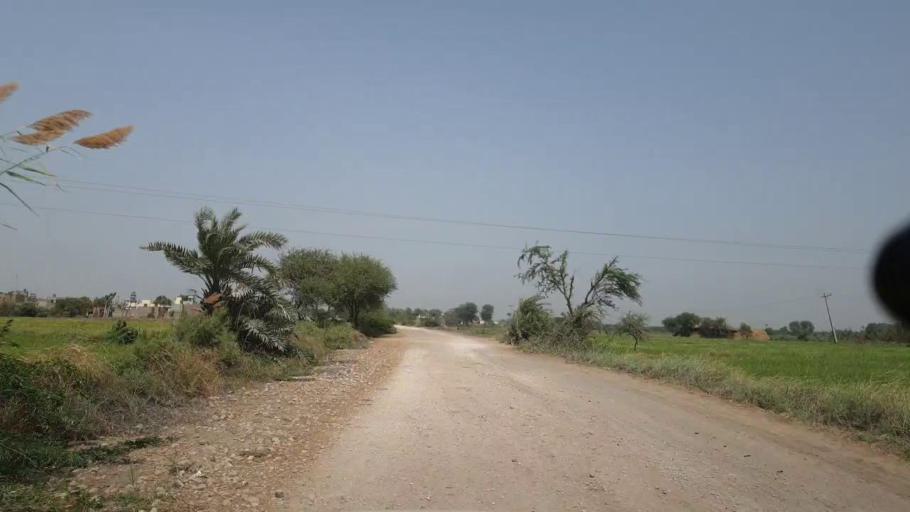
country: PK
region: Sindh
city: Matli
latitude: 25.0593
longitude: 68.7074
